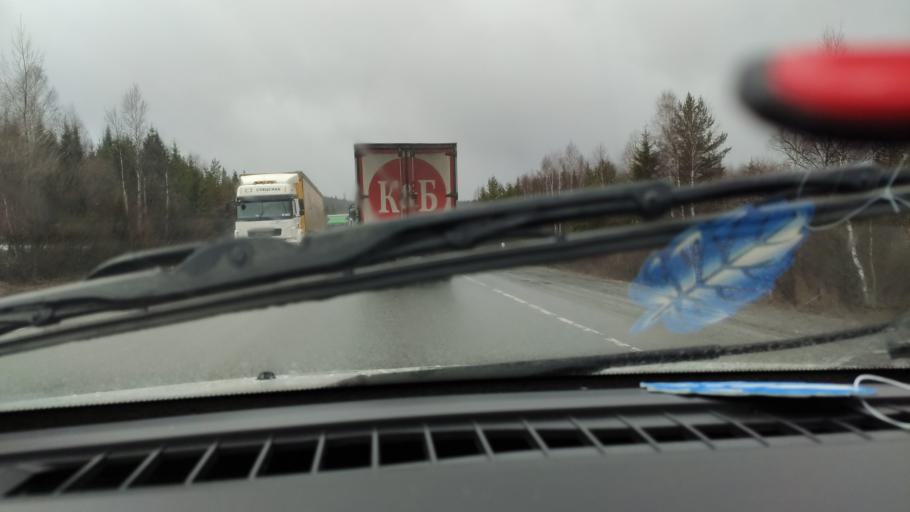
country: RU
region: Sverdlovsk
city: Arti
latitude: 56.7891
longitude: 58.5831
